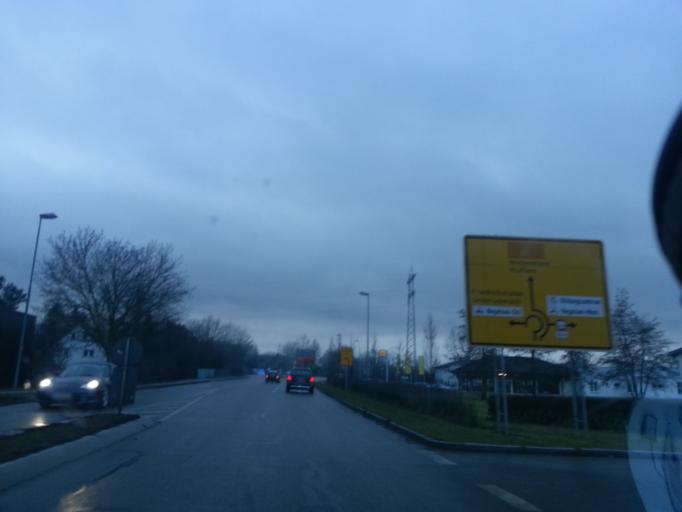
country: DE
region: Baden-Wuerttemberg
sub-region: Tuebingen Region
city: Markdorf
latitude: 47.7127
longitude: 9.3984
